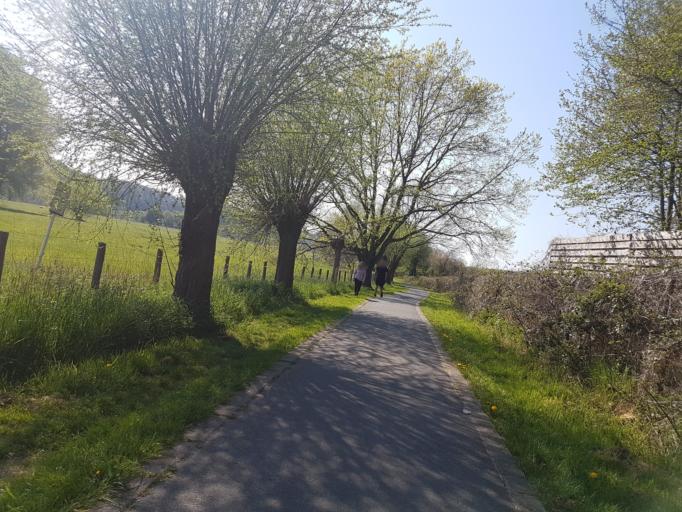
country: DE
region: North Rhine-Westphalia
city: Hattingen
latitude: 51.4137
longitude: 7.2328
